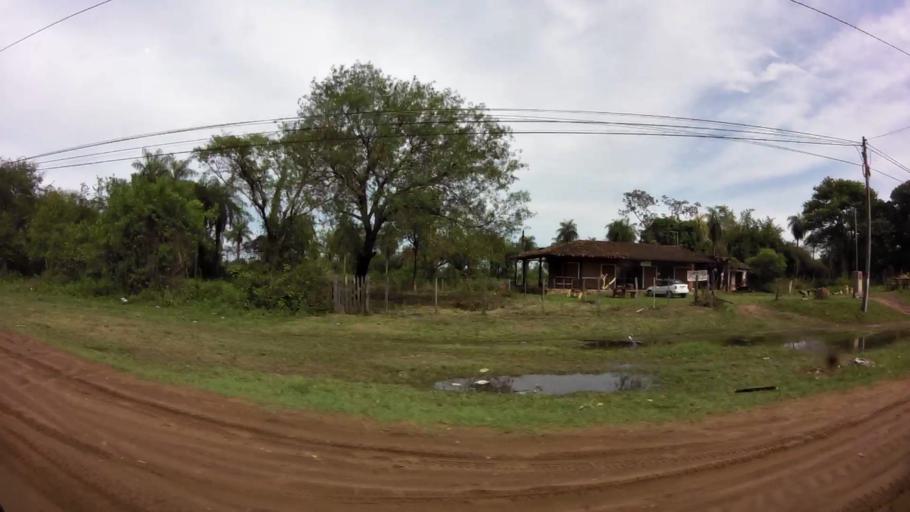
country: PY
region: Central
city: Limpio
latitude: -25.1567
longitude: -57.4739
